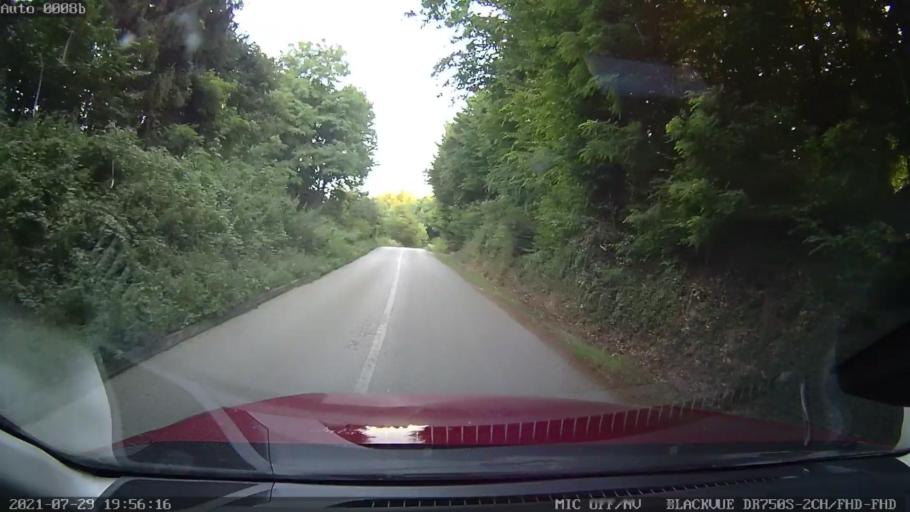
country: HR
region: Varazdinska
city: Jalzabet
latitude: 46.2501
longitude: 16.4721
